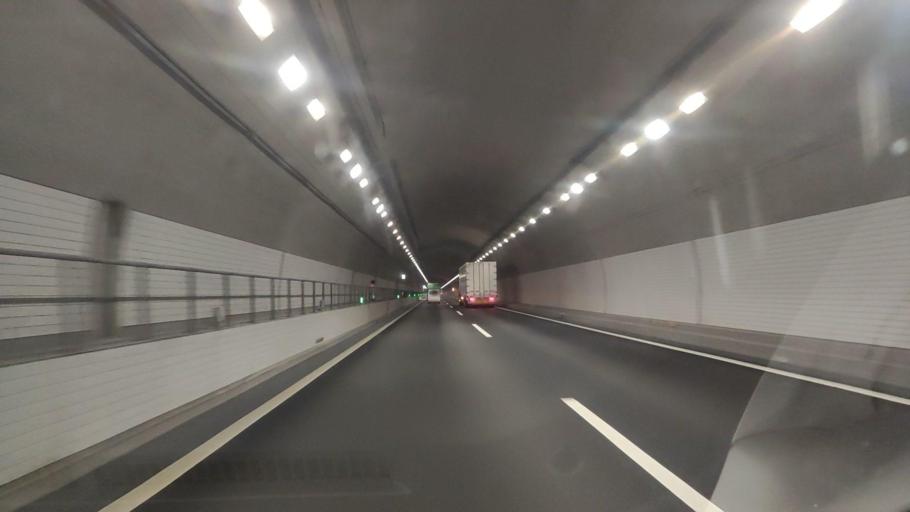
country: JP
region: Tokyo
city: Hachioji
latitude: 35.5734
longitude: 139.3011
